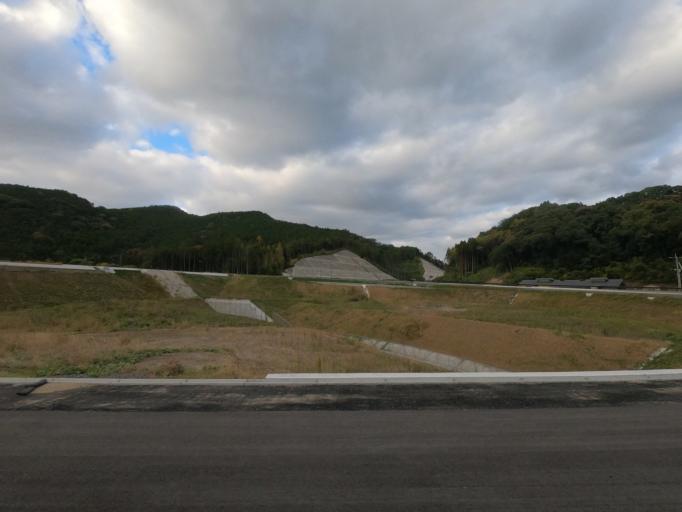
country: JP
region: Kumamoto
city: Minamata
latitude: 32.2108
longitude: 130.4256
